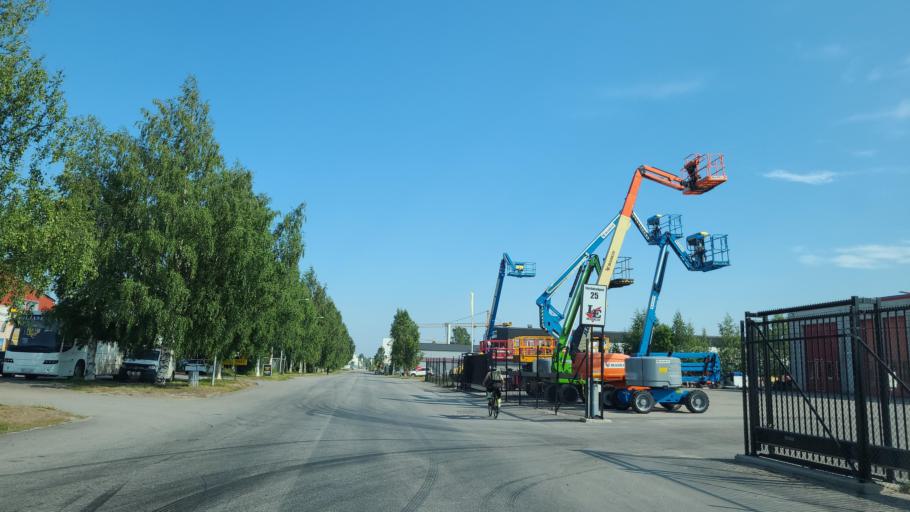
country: SE
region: Vaesterbotten
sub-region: Umea Kommun
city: Umea
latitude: 63.8448
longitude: 20.2204
